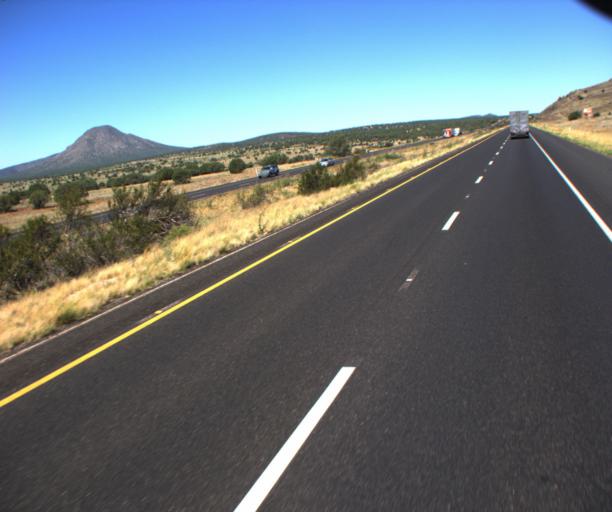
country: US
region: Arizona
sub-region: Yavapai County
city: Paulden
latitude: 35.2431
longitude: -112.6711
